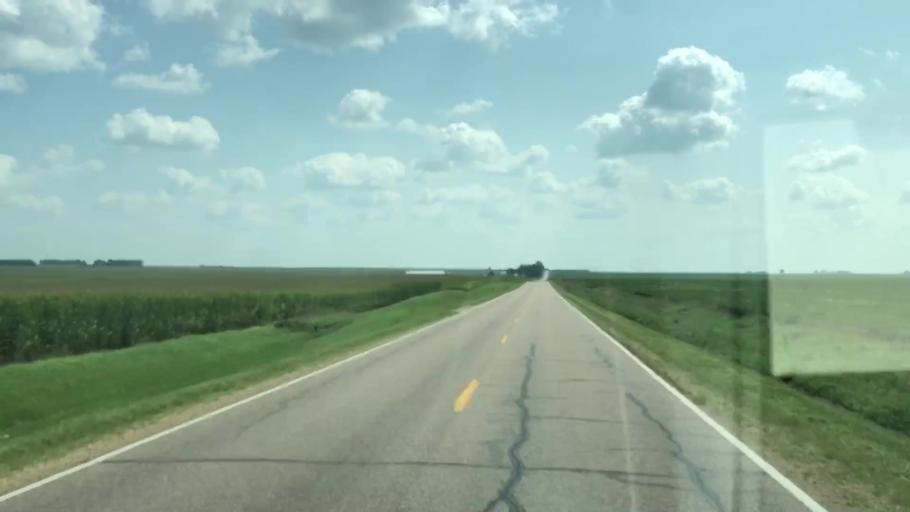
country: US
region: Iowa
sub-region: O'Brien County
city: Sheldon
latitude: 43.1622
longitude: -95.8019
